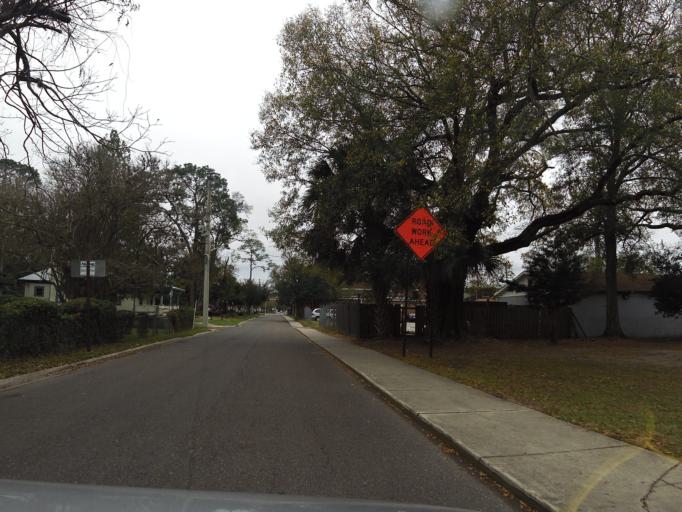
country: US
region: Florida
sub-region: Duval County
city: Jacksonville
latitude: 30.3461
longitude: -81.6842
